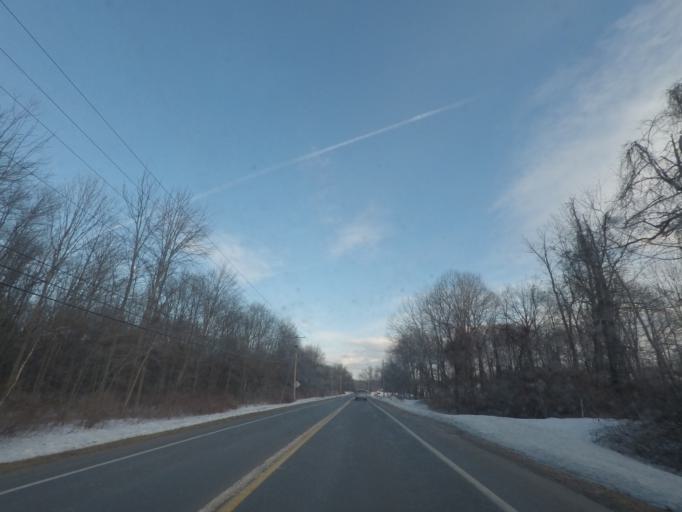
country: US
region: New York
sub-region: Saratoga County
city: Country Knolls
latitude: 42.8399
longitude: -73.7903
